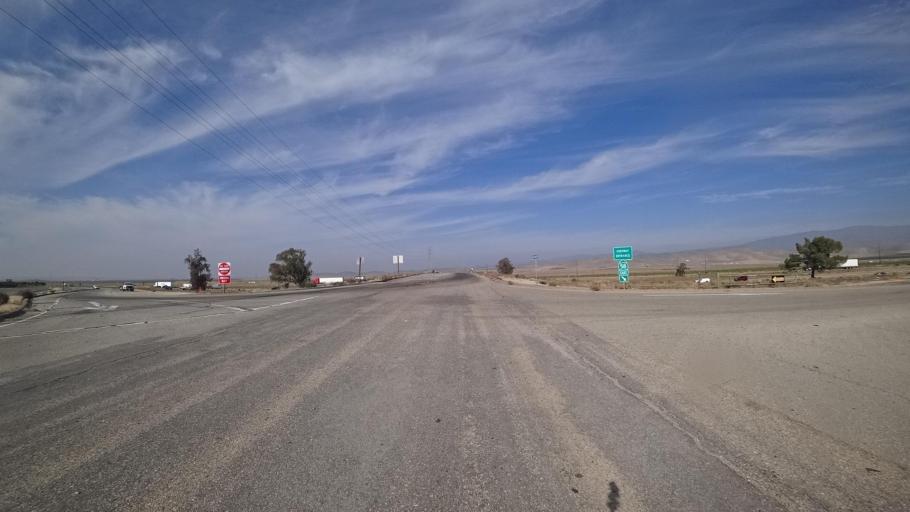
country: US
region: California
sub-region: Kern County
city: Arvin
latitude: 35.3286
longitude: -118.8075
